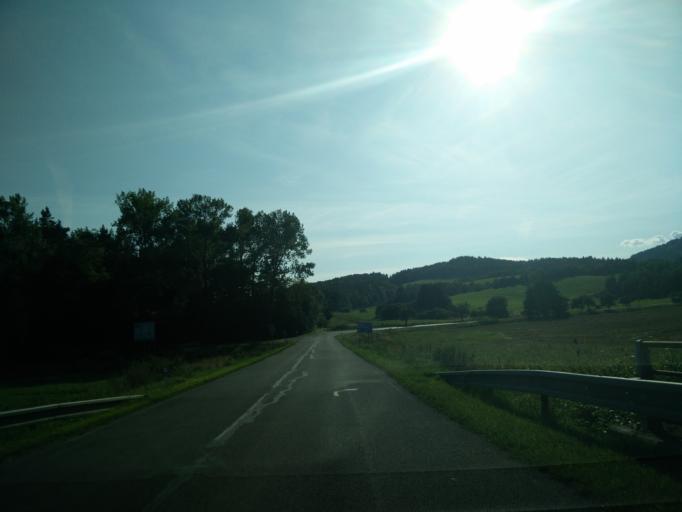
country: SK
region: Nitriansky
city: Handlova
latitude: 48.8764
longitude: 18.7404
